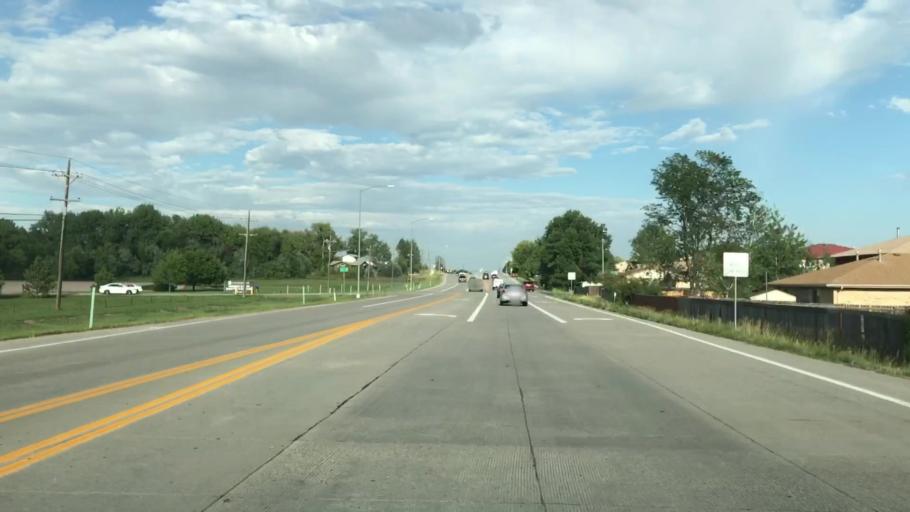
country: US
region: Colorado
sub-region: Boulder County
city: Longmont
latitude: 40.2032
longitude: -105.1118
